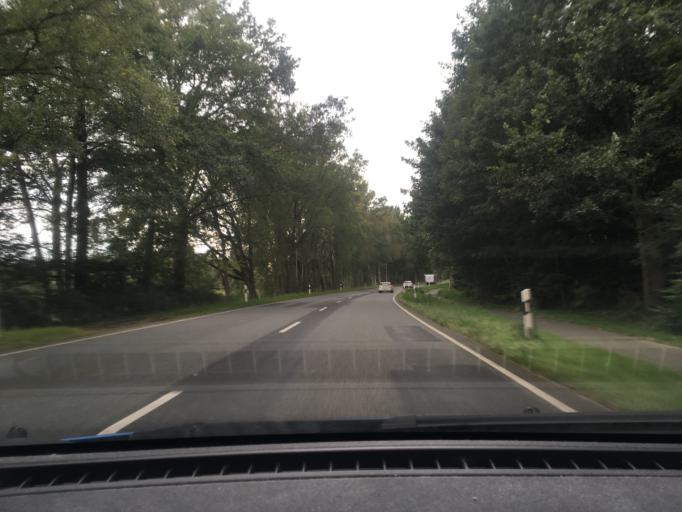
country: DE
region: Lower Saxony
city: Eschede
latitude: 52.7509
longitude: 10.2650
